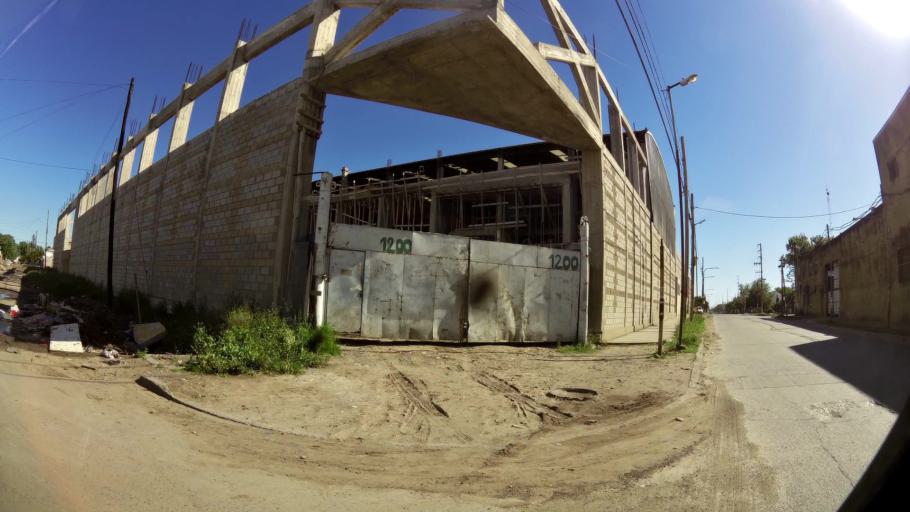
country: AR
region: Buenos Aires
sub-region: Partido de Quilmes
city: Quilmes
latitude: -34.7621
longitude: -58.3035
